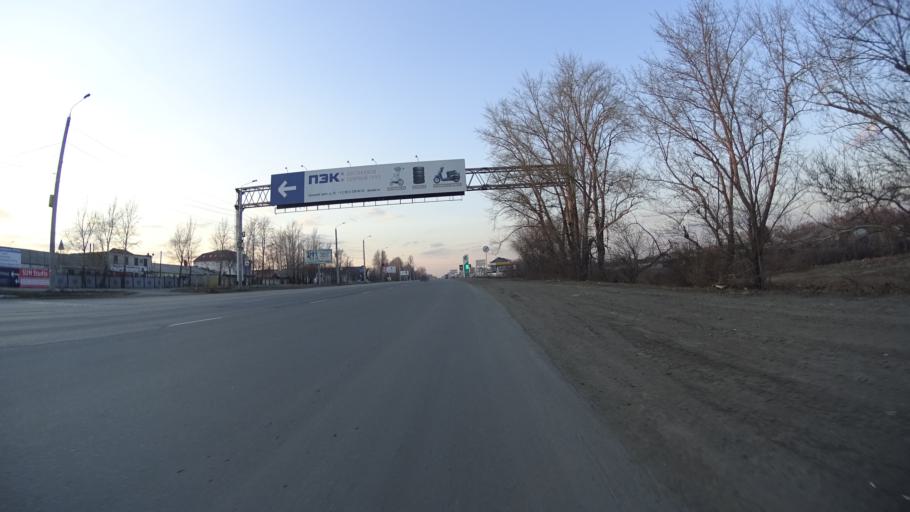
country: RU
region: Chelyabinsk
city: Novosineglazovskiy
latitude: 55.0865
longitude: 61.3885
